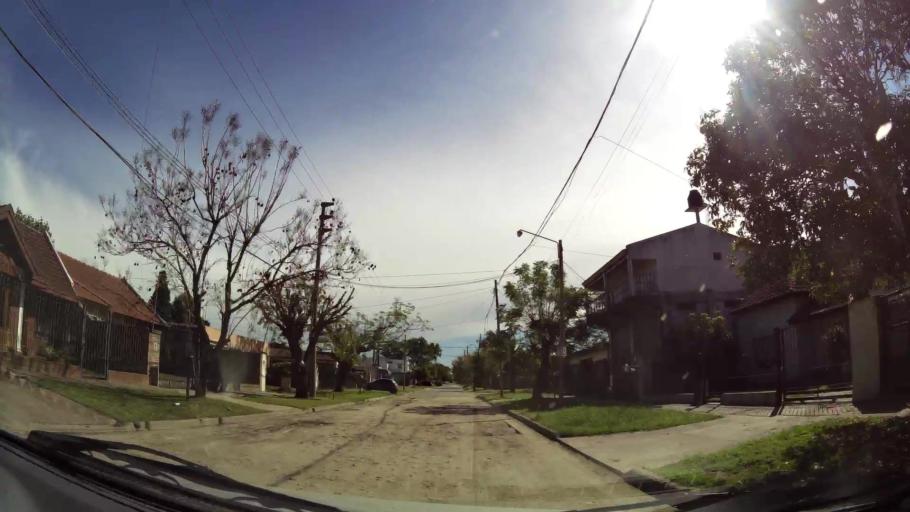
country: AR
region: Buenos Aires
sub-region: Partido de Almirante Brown
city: Adrogue
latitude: -34.8005
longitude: -58.3558
